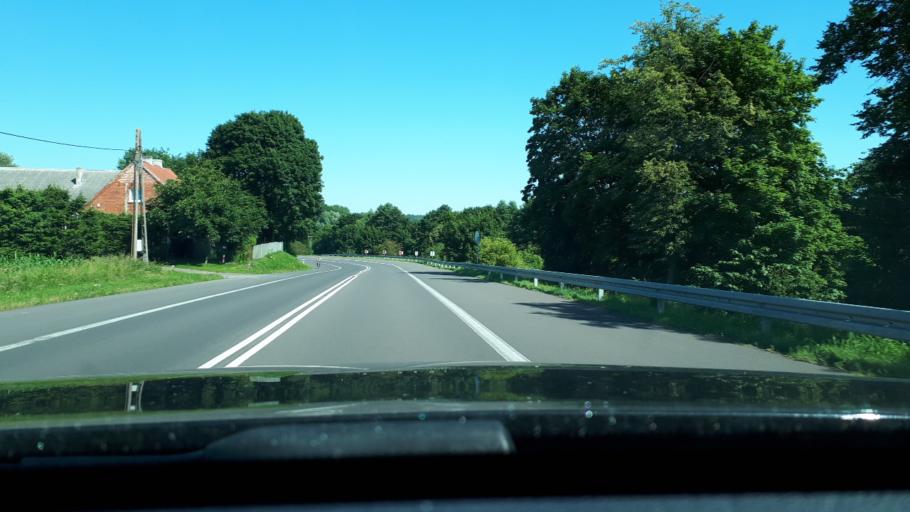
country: PL
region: Warmian-Masurian Voivodeship
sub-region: Powiat ostrodzki
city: Ostroda
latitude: 53.6674
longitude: 20.0385
